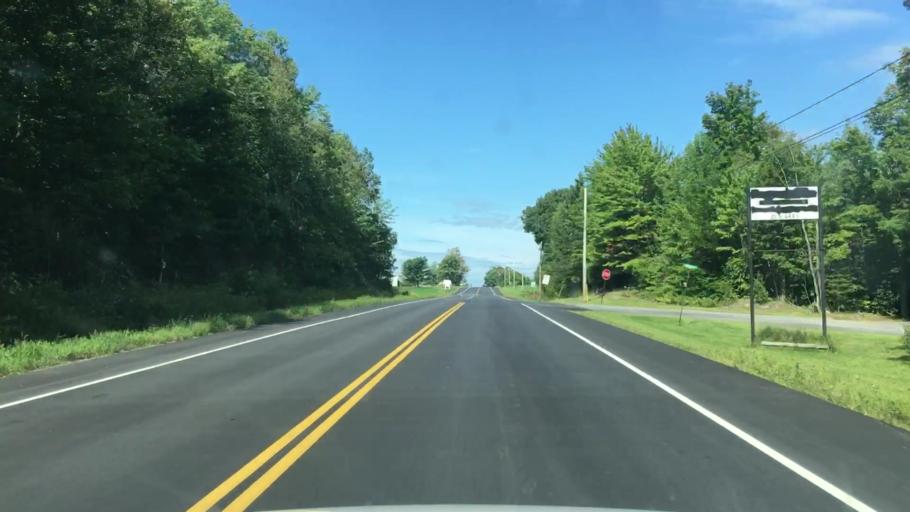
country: US
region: Maine
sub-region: Penobscot County
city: Corinna
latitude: 44.9515
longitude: -69.2526
